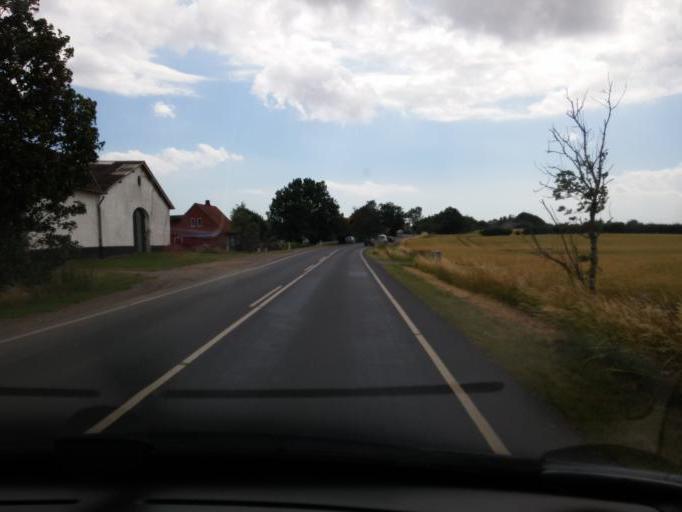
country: DK
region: South Denmark
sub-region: Langeland Kommune
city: Rudkobing
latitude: 54.9158
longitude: 10.7328
